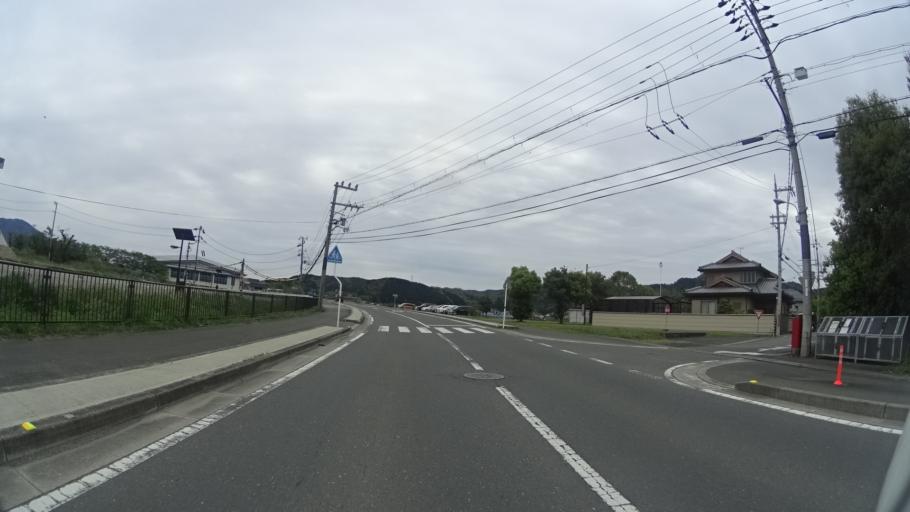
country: JP
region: Kyoto
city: Kameoka
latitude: 35.0757
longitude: 135.5365
